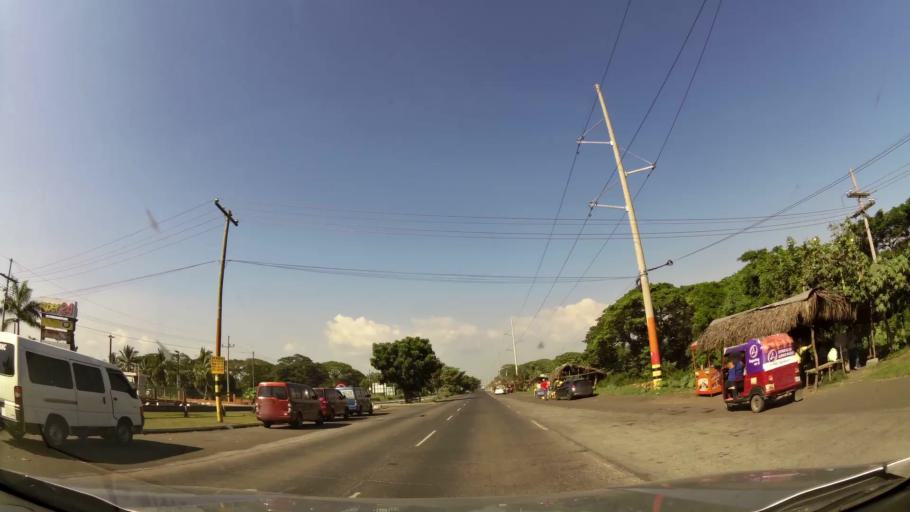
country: GT
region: Escuintla
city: Puerto San Jose
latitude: 13.9419
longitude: -90.7885
